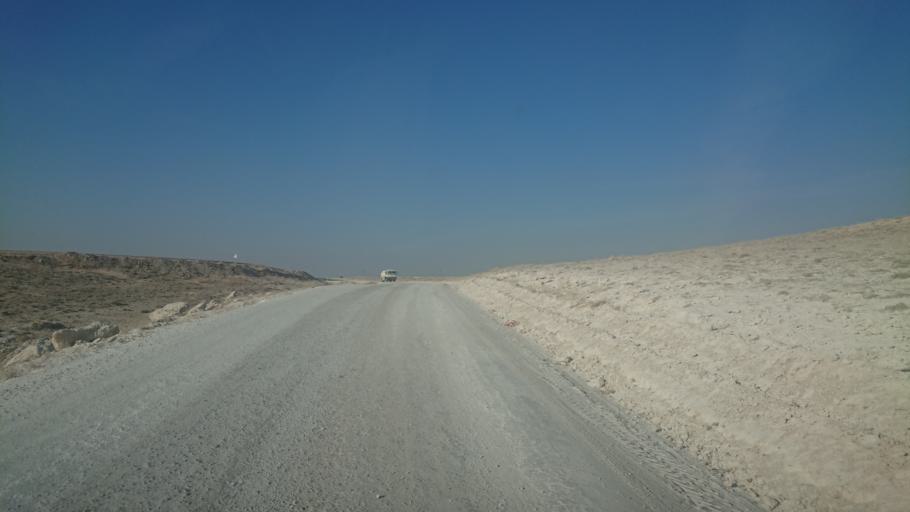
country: TR
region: Aksaray
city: Sultanhani
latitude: 38.0841
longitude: 33.6152
